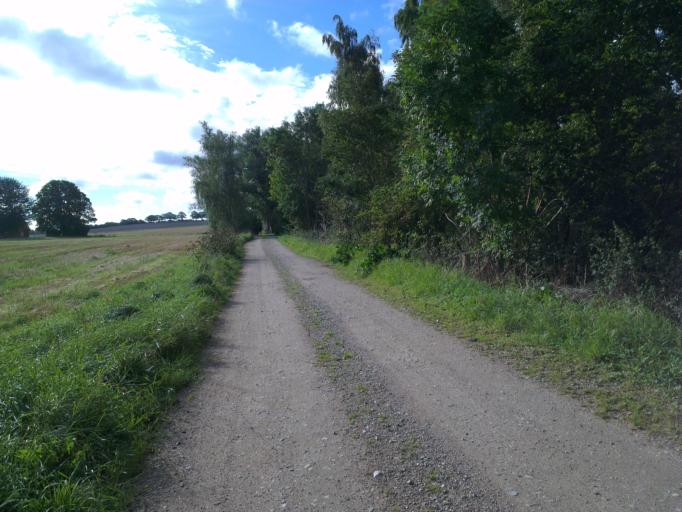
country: DK
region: Capital Region
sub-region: Frederikssund Kommune
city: Frederikssund
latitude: 55.8002
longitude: 12.0911
